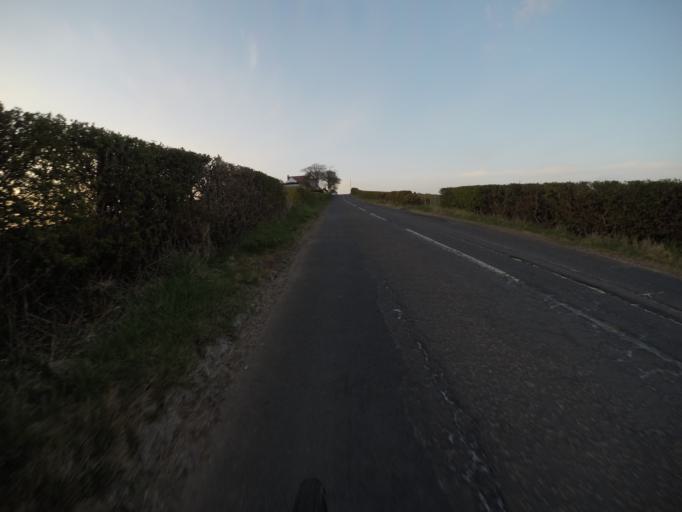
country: GB
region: Scotland
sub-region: South Ayrshire
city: Dundonald
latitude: 55.5532
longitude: -4.6187
